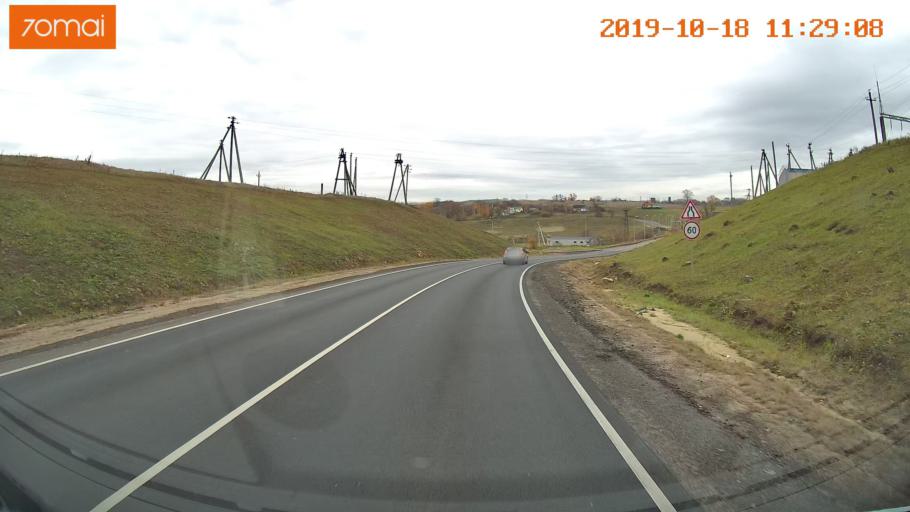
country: RU
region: Rjazan
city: Oktyabr'skiy
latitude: 54.1577
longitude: 38.6727
